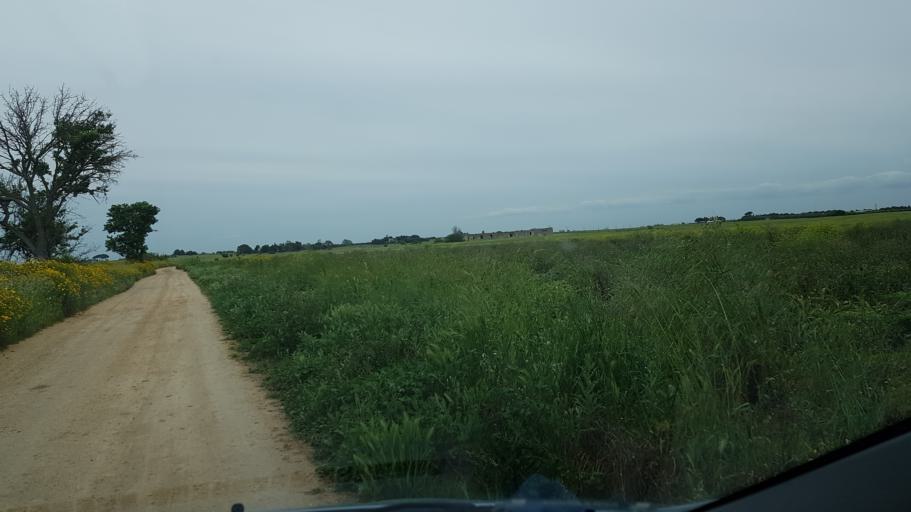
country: IT
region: Apulia
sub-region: Provincia di Brindisi
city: Brindisi
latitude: 40.6598
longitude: 17.8804
